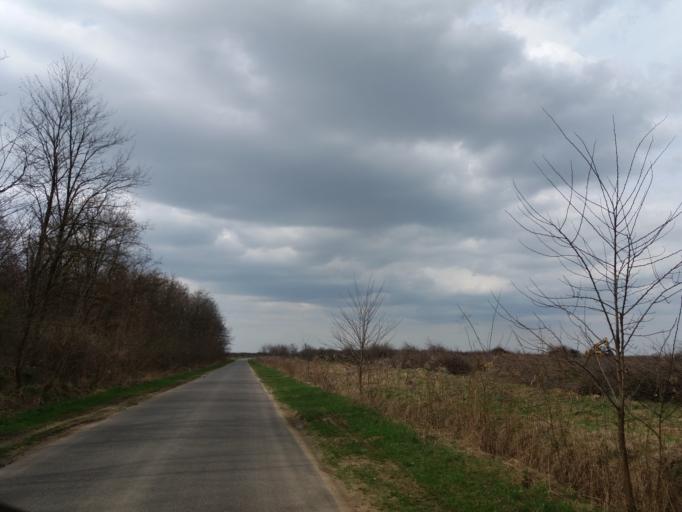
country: HU
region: Szabolcs-Szatmar-Bereg
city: Nyirtass
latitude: 48.0898
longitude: 22.0337
